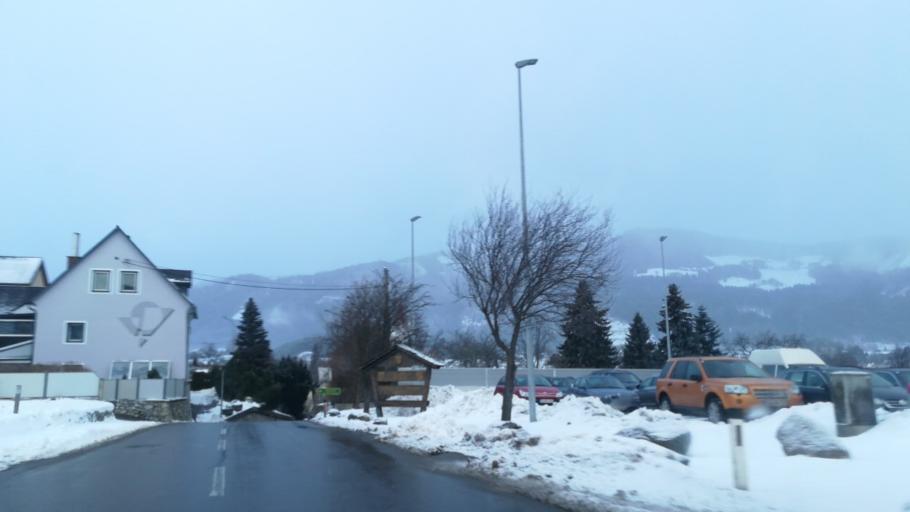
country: AT
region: Styria
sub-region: Politischer Bezirk Murtal
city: Poels
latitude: 47.2177
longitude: 14.5813
